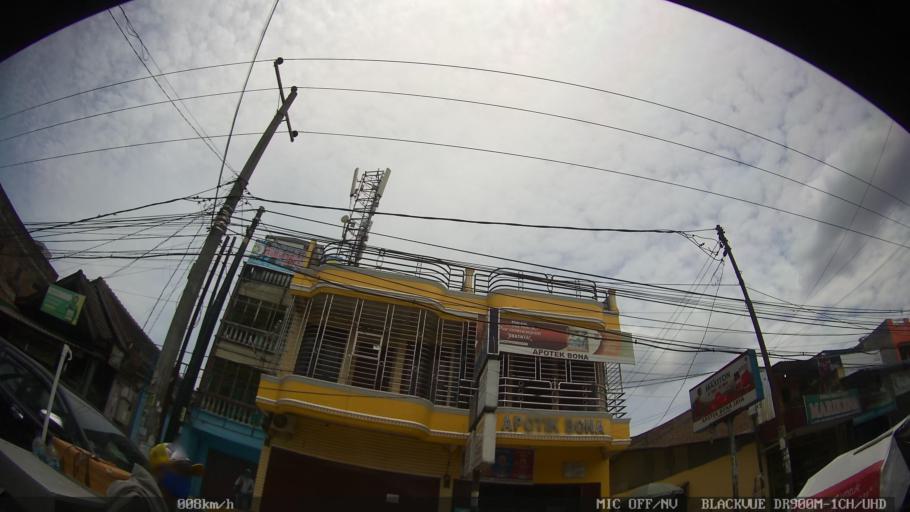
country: ID
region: North Sumatra
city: Deli Tua
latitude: 3.5394
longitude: 98.6529
